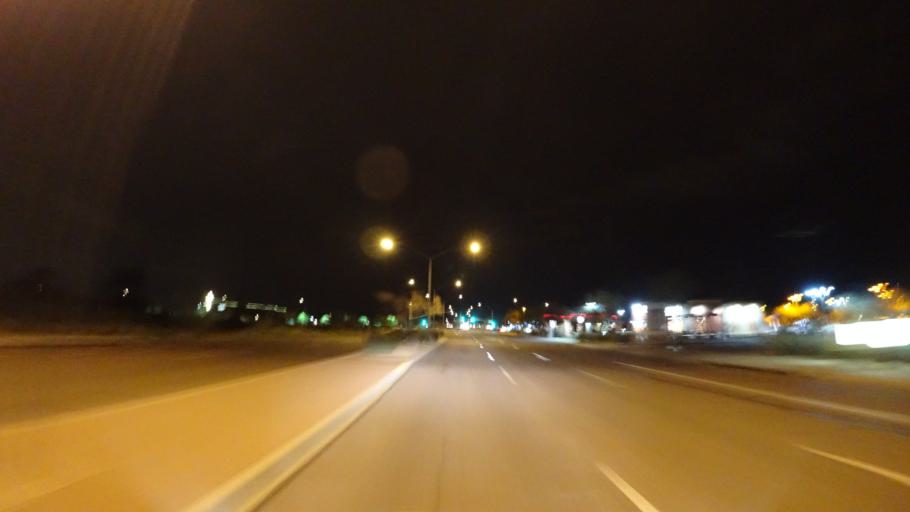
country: US
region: Arizona
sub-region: Pinal County
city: Apache Junction
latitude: 33.3882
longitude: -111.6153
